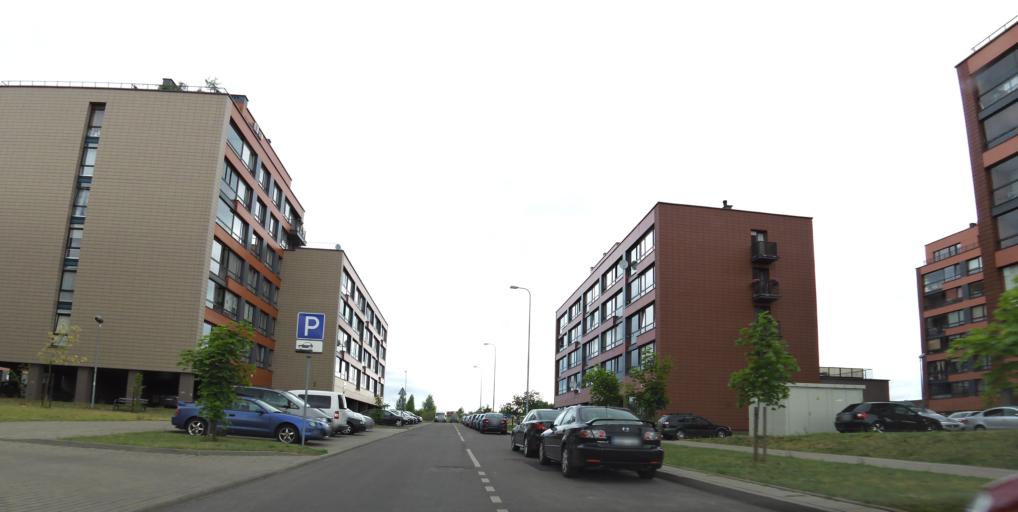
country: LT
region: Vilnius County
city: Pilaite
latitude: 54.7118
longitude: 25.1798
